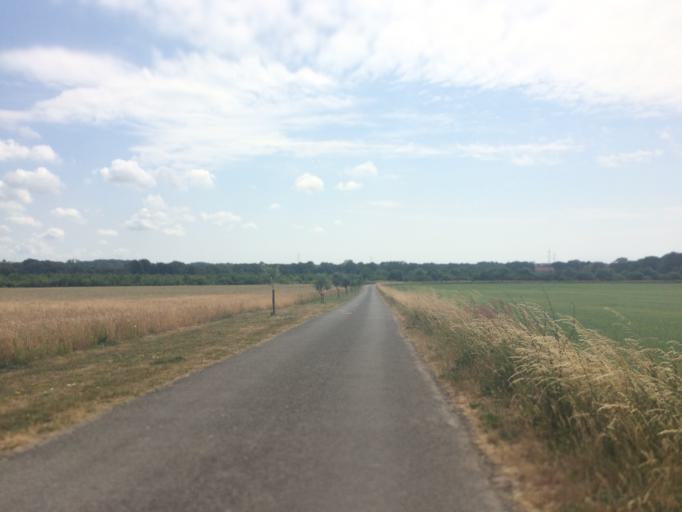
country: DK
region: Capital Region
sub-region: Bornholm Kommune
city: Ronne
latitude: 55.1737
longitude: 14.7256
